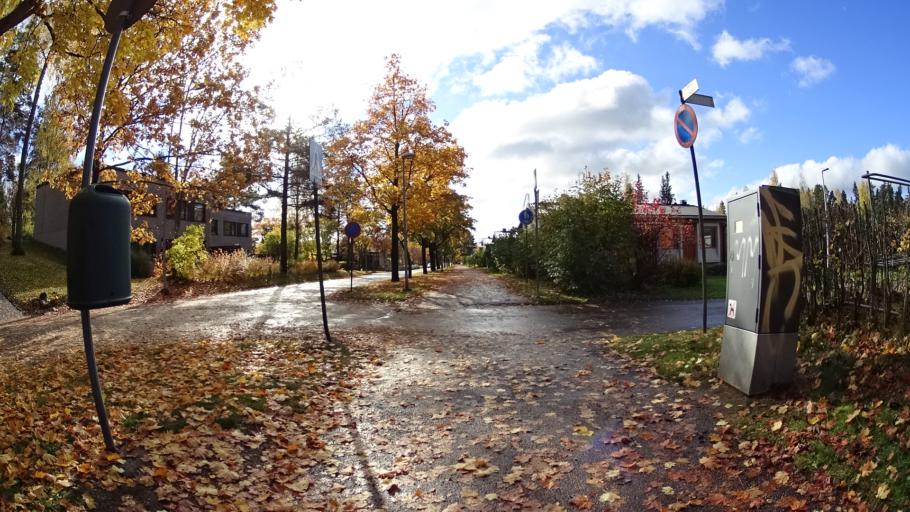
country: FI
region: Uusimaa
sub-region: Helsinki
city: Kilo
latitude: 60.2714
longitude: 24.8209
